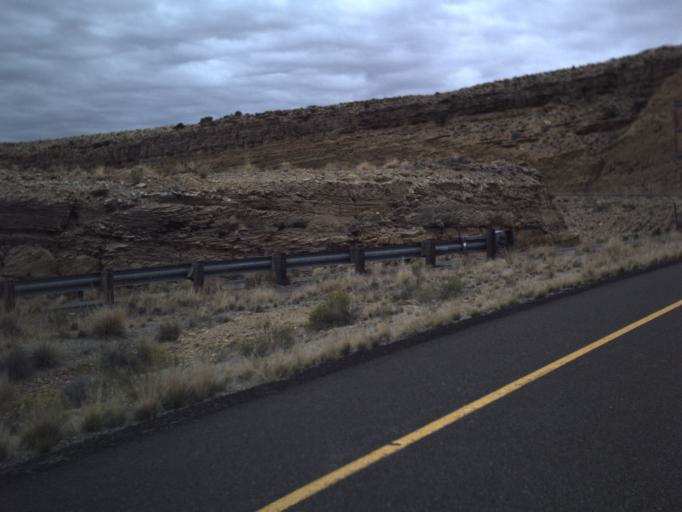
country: US
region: Utah
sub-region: Emery County
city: Castle Dale
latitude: 38.9358
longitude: -110.4777
